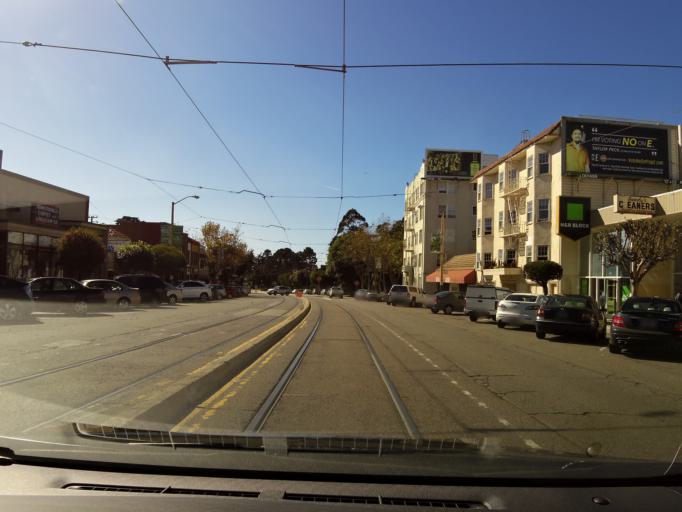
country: US
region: California
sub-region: San Mateo County
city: Daly City
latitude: 37.7373
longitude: -122.4699
